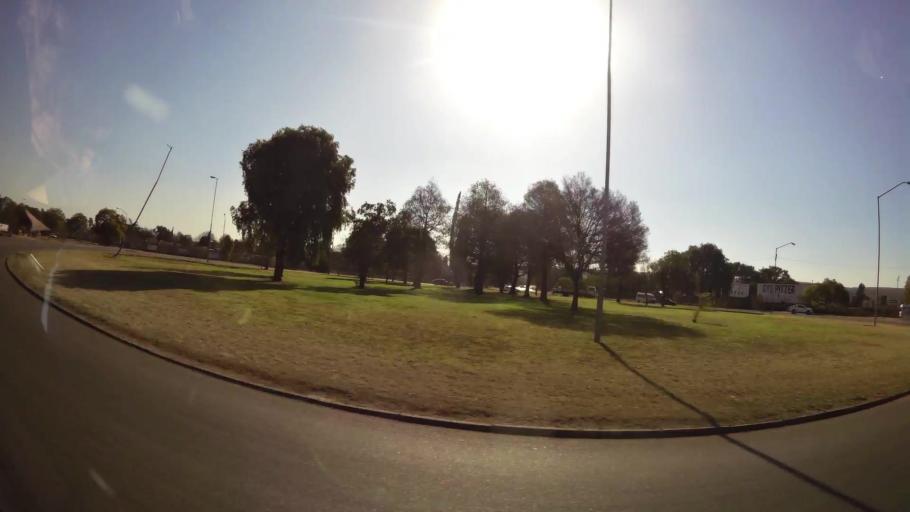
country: ZA
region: Gauteng
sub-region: City of Tshwane Metropolitan Municipality
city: Pretoria
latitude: -25.7128
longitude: 28.2577
